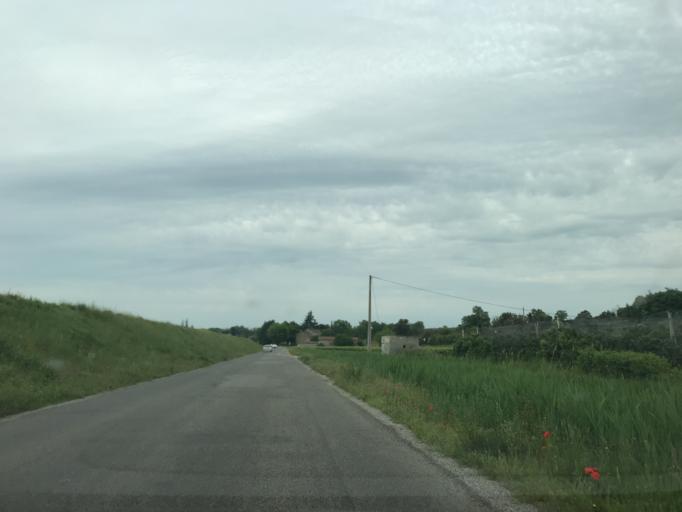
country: FR
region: Provence-Alpes-Cote d'Azur
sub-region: Departement des Alpes-de-Haute-Provence
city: Volx
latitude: 43.8413
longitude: 5.8298
